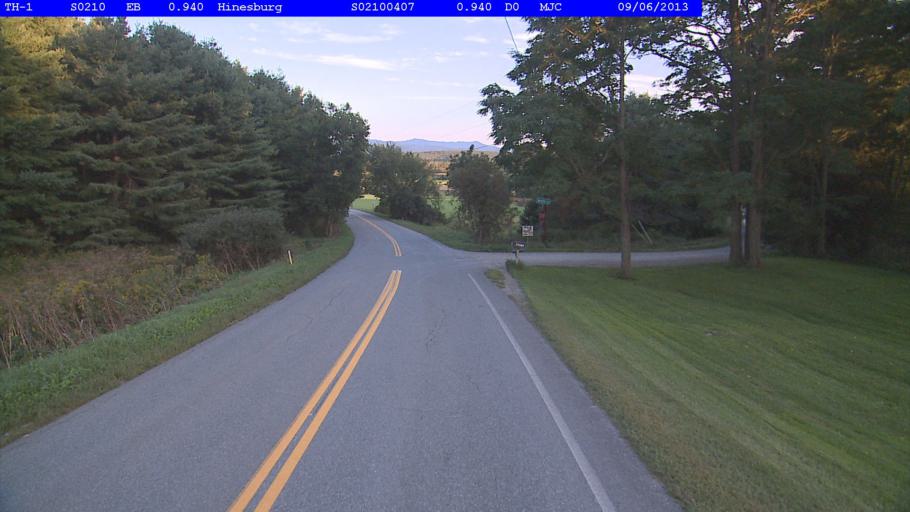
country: US
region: Vermont
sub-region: Chittenden County
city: Hinesburg
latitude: 44.3512
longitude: -73.1518
